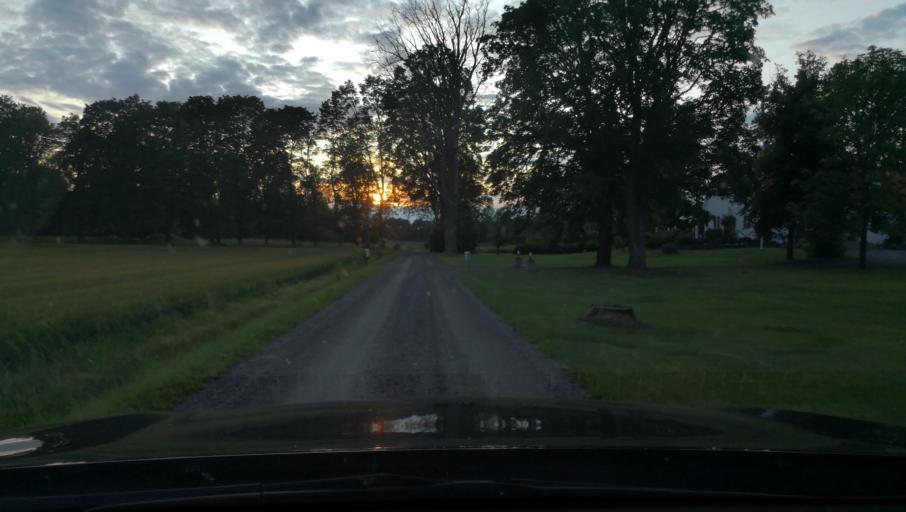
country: SE
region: Uppsala
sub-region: Osthammars Kommun
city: Bjorklinge
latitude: 60.0559
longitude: 17.6231
